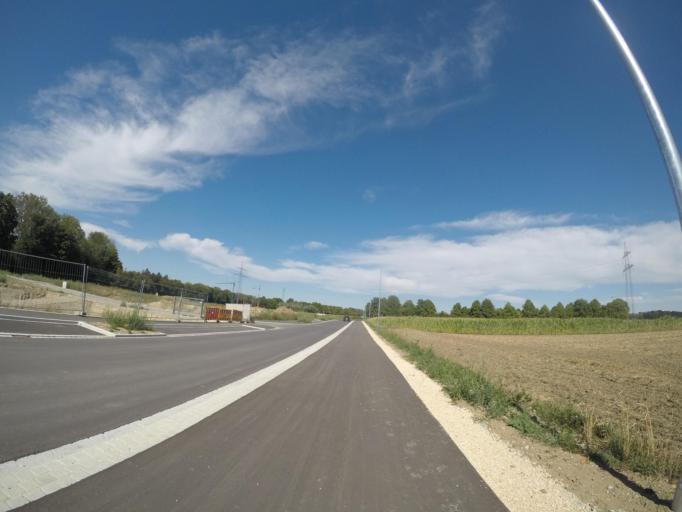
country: DE
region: Bavaria
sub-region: Swabia
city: Senden
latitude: 48.3313
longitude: 10.0275
